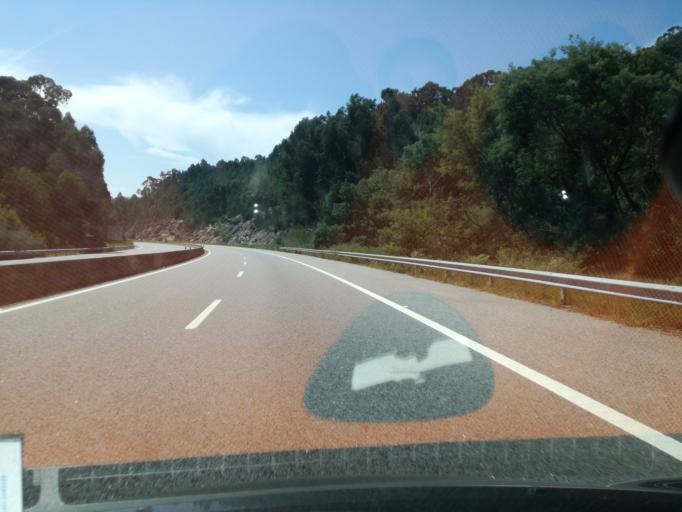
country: PT
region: Viana do Castelo
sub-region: Viana do Castelo
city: Meadela
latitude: 41.7499
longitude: -8.7996
